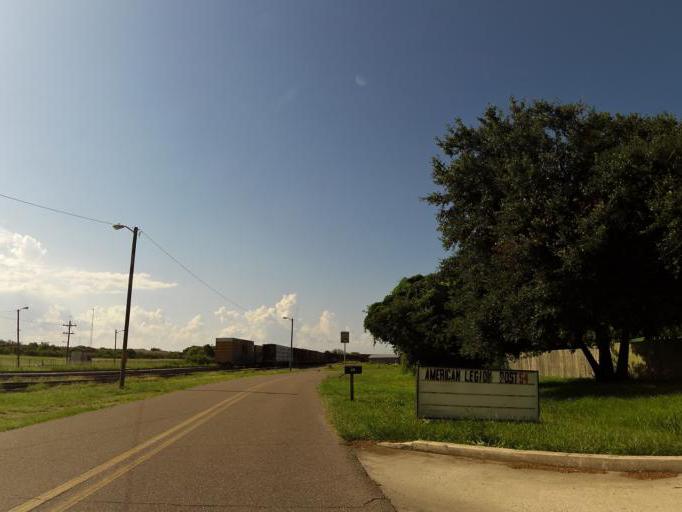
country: US
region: Florida
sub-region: Nassau County
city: Fernandina Beach
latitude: 30.6630
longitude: -81.4639
